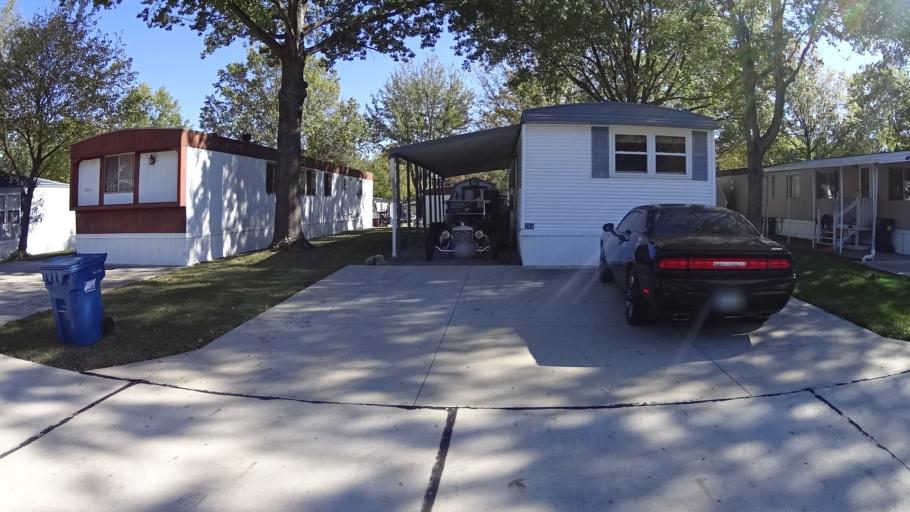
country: US
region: Ohio
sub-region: Lorain County
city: Amherst
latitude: 41.3891
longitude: -82.2514
